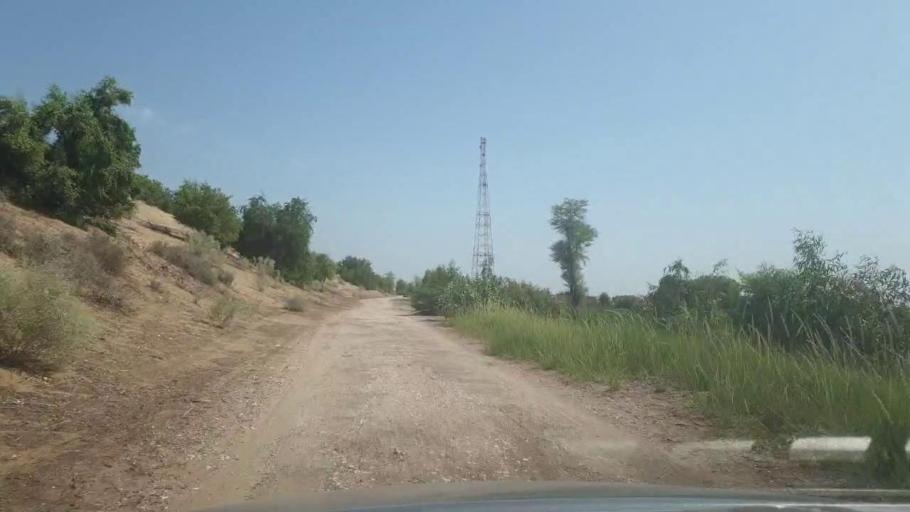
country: PK
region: Sindh
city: Khairpur
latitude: 27.3994
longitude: 69.0795
